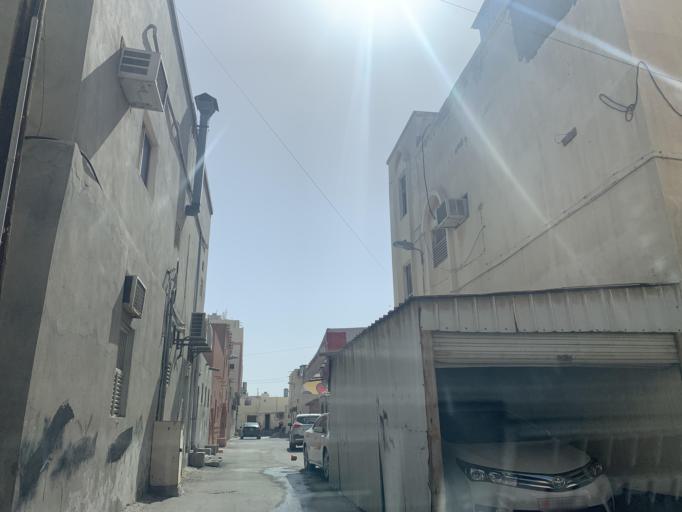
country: BH
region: Northern
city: Sitrah
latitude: 26.1626
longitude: 50.6110
